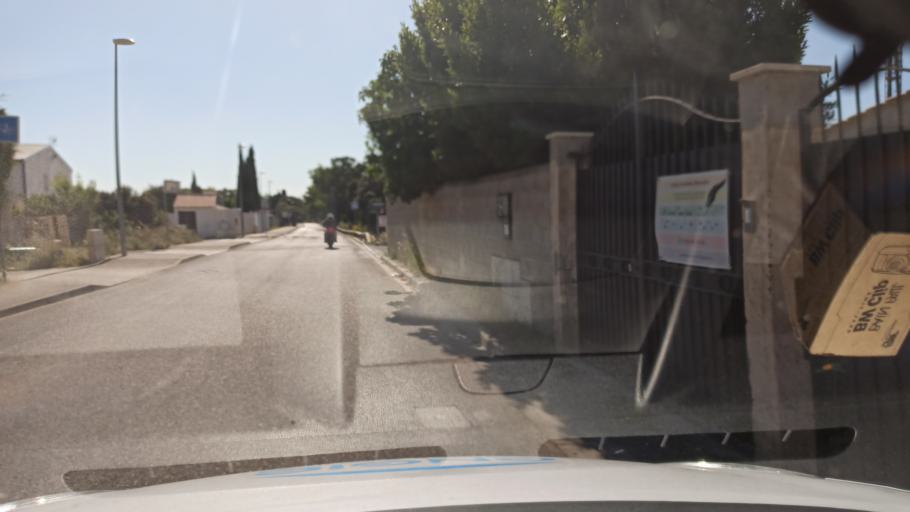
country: FR
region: Provence-Alpes-Cote d'Azur
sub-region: Departement du Vaucluse
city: Morieres-les-Avignon
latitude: 43.9578
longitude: 4.8991
